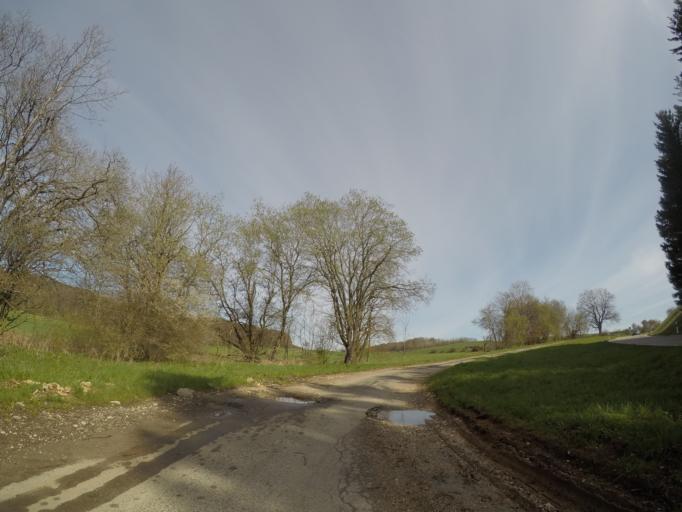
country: DE
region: Baden-Wuerttemberg
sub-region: Regierungsbezirk Stuttgart
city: Hohenstadt
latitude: 48.5321
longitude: 9.6531
